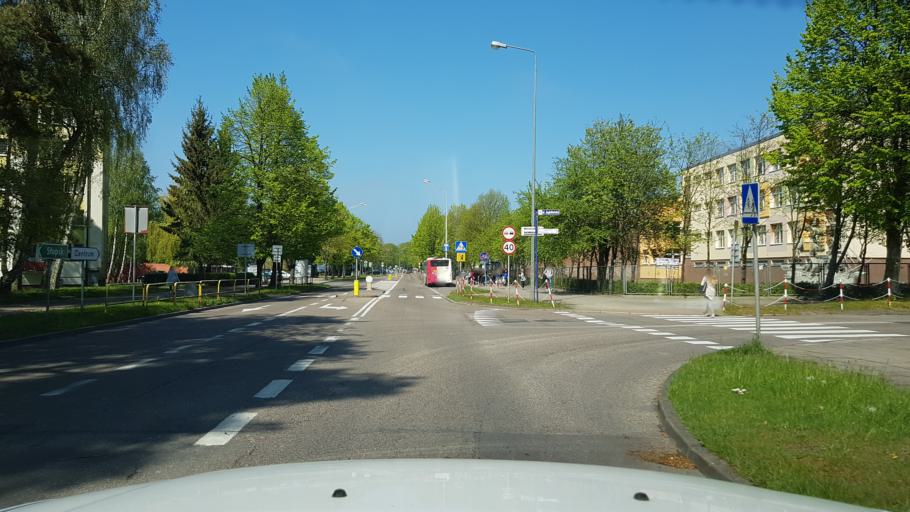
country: PL
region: Pomeranian Voivodeship
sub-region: Powiat slupski
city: Ustka
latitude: 54.5775
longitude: 16.8675
